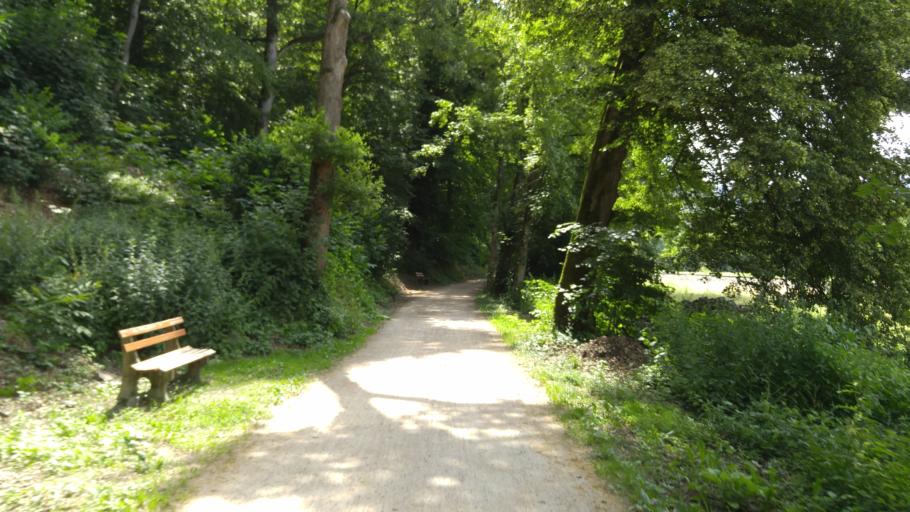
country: DE
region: Baden-Wuerttemberg
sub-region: Freiburg Region
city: Muenstertal/Schwarzwald
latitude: 47.8702
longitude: 7.7431
